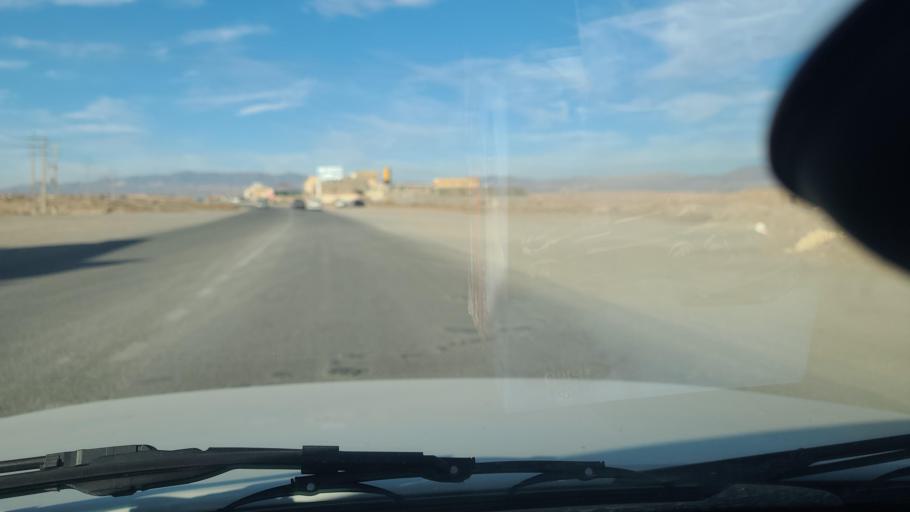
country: IR
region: Razavi Khorasan
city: Sabzevar
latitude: 36.2249
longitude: 57.6518
